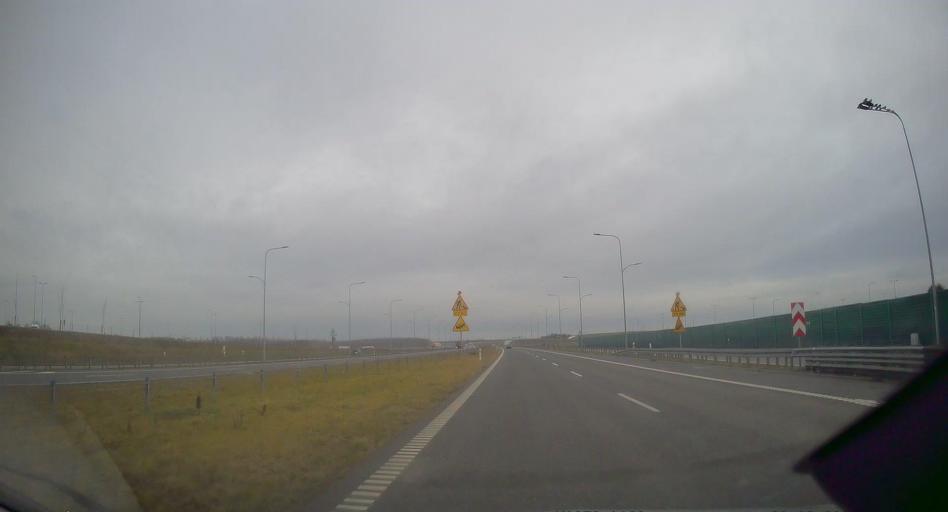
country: PL
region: Silesian Voivodeship
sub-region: Powiat czestochowski
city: Mykanow
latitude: 50.8761
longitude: 19.1398
